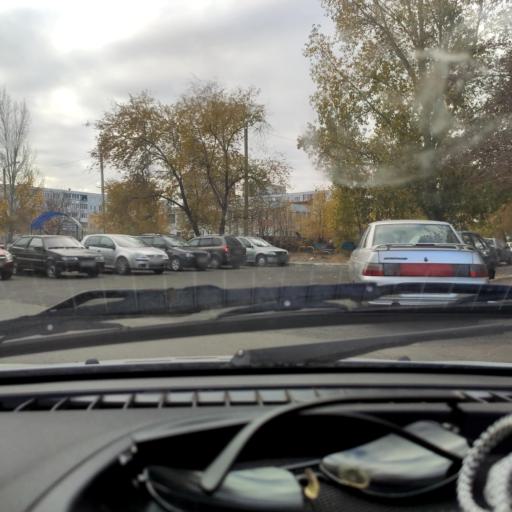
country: RU
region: Samara
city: Zhigulevsk
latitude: 53.4735
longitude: 49.5338
